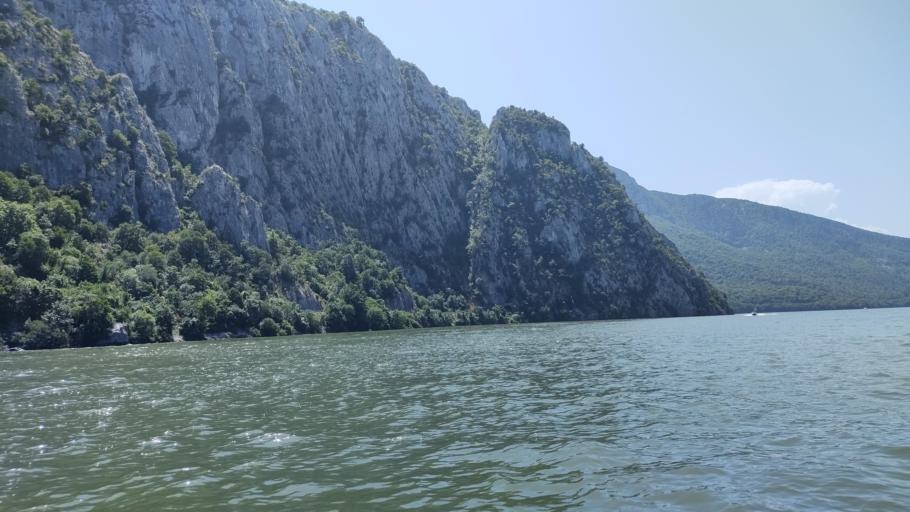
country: RO
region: Mehedinti
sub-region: Comuna Dubova
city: Dubova
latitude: 44.6177
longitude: 22.2730
